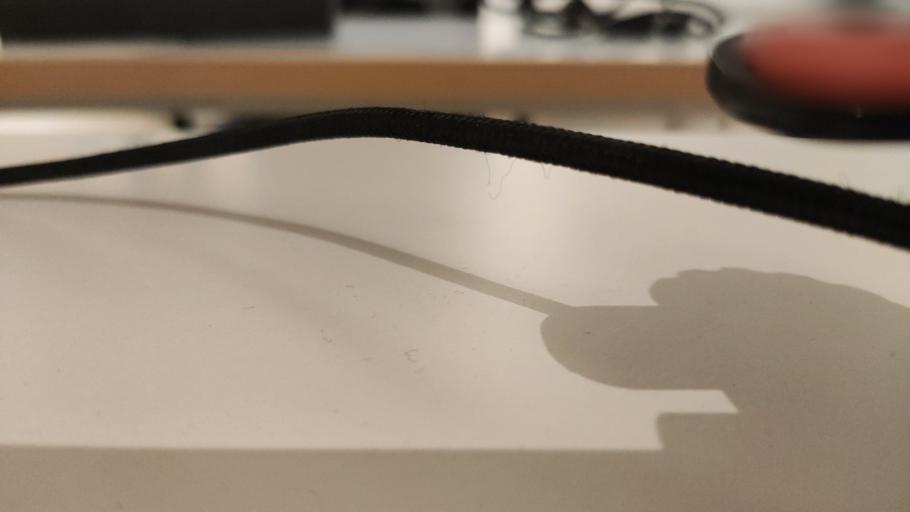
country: RU
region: Moskovskaya
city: Dorokhovo
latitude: 55.4573
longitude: 36.3535
